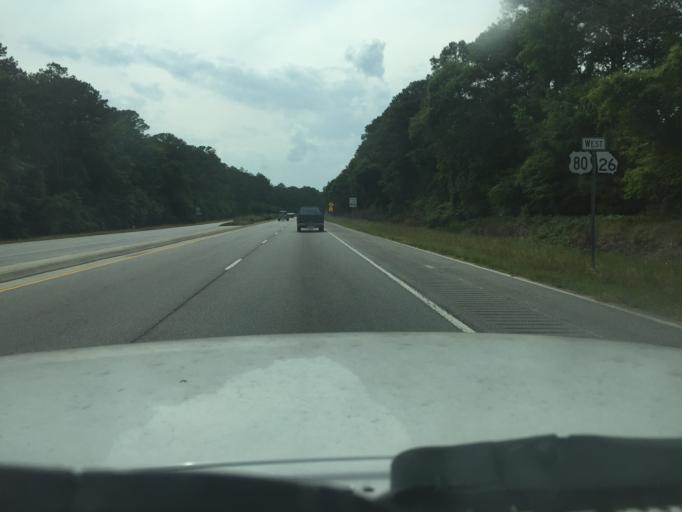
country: US
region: Georgia
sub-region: Chatham County
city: Wilmington Island
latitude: 32.0317
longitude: -80.9739
